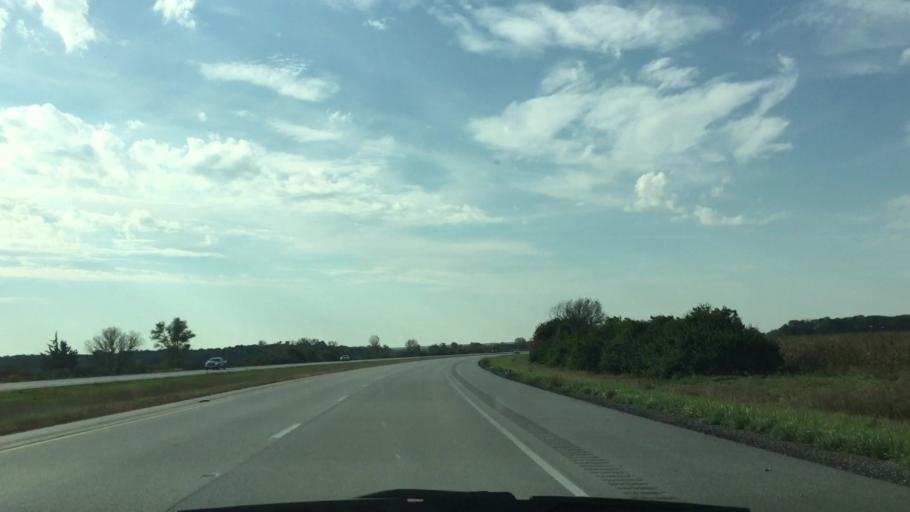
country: US
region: Illinois
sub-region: Whiteside County
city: Erie
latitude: 41.6023
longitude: -90.1922
